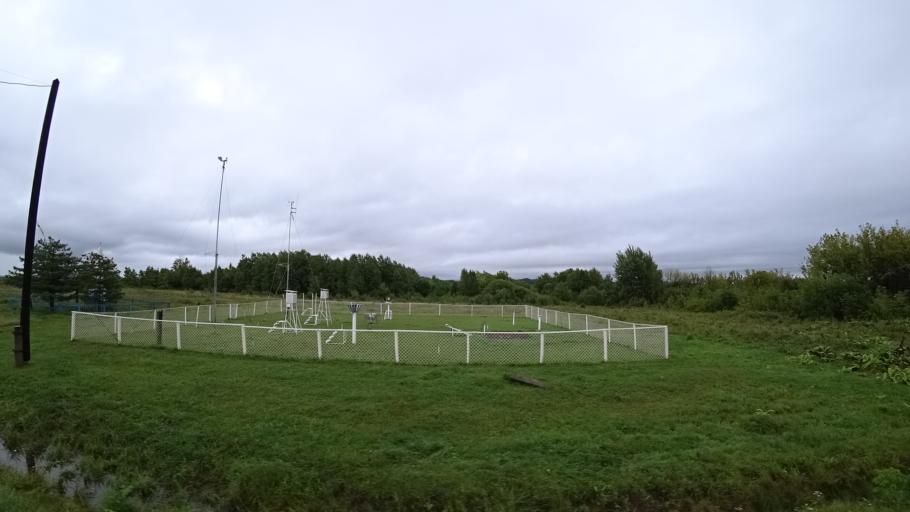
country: RU
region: Primorskiy
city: Monastyrishche
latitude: 44.2700
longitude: 132.4205
